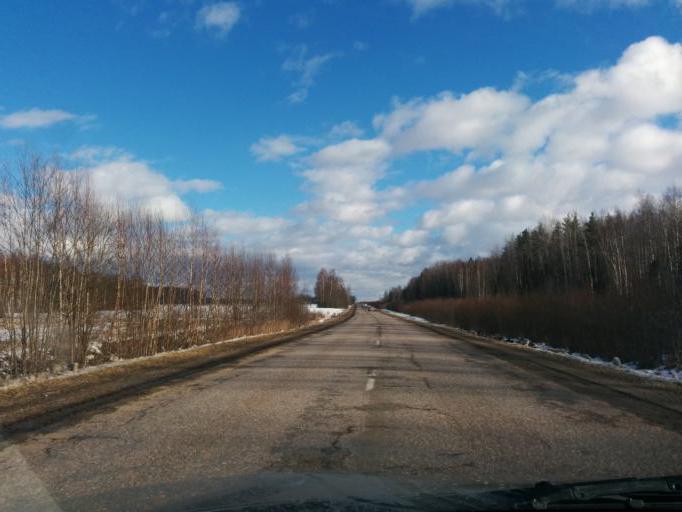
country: LV
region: Balvu Rajons
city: Balvi
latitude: 57.1628
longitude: 27.1506
